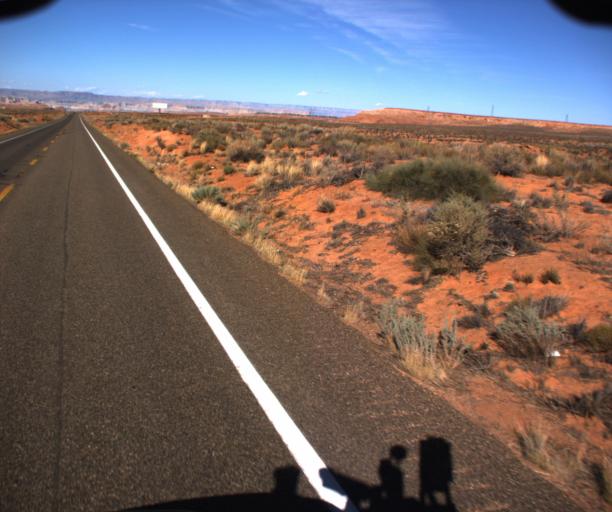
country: US
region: Arizona
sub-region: Coconino County
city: Page
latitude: 36.8667
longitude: -111.5037
